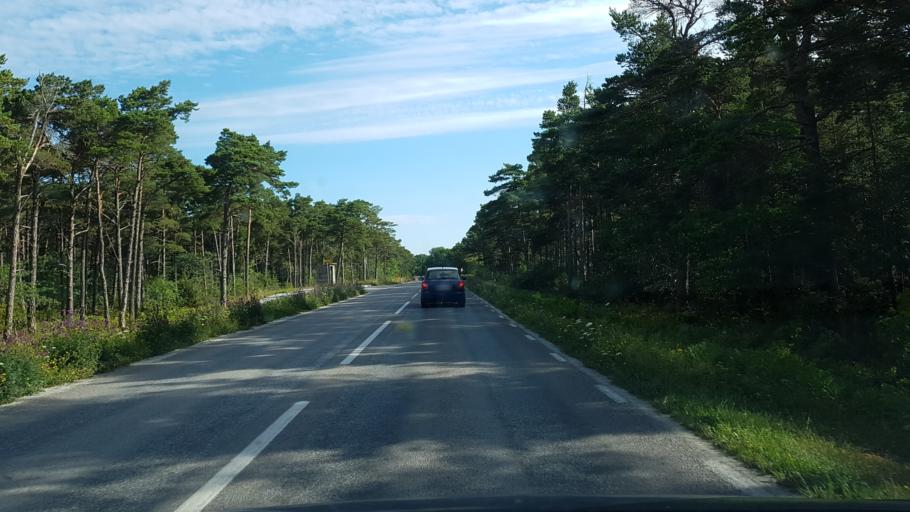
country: SE
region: Gotland
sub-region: Gotland
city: Visby
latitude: 57.7089
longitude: 18.3822
